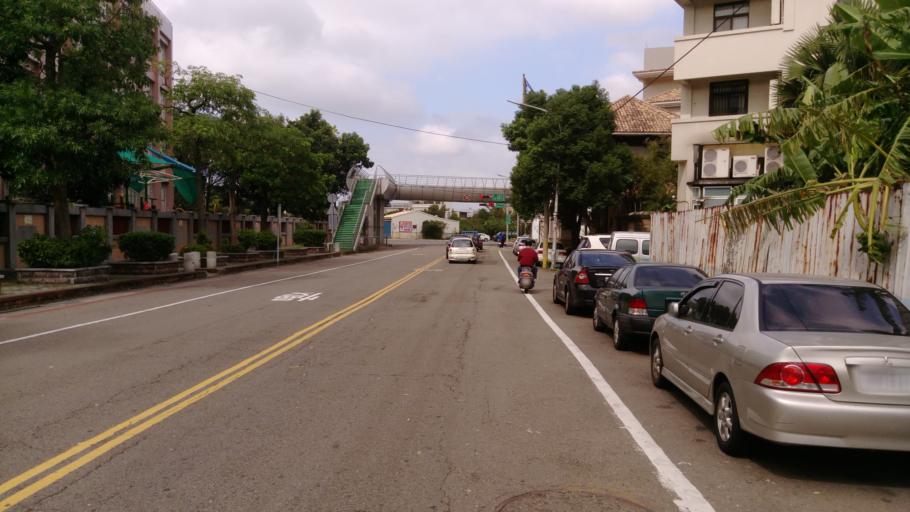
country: TW
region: Taiwan
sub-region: Hsinchu
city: Hsinchu
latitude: 24.7981
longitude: 120.9505
